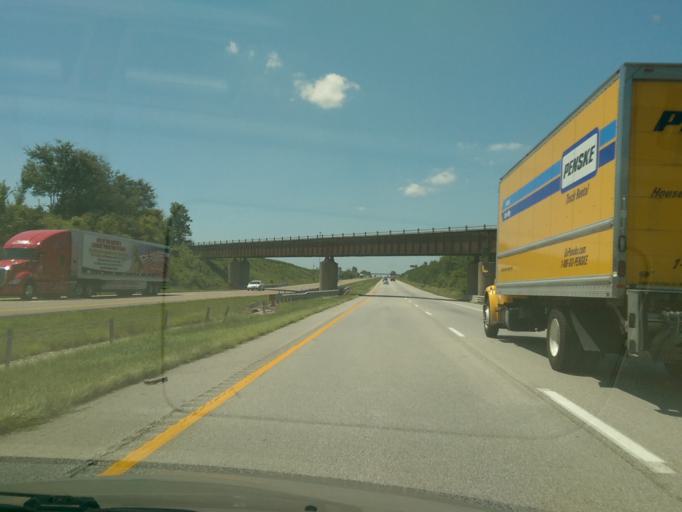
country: US
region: Missouri
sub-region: Cooper County
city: Boonville
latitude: 38.9353
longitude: -92.8007
